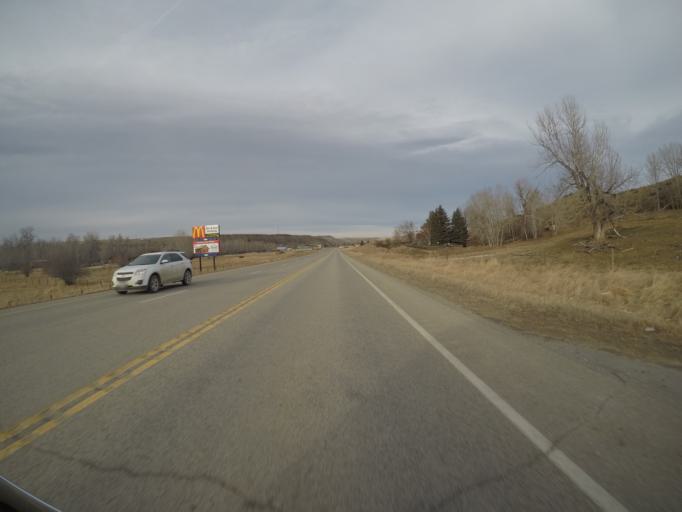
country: US
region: Montana
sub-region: Stillwater County
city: Absarokee
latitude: 45.5042
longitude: -109.4487
